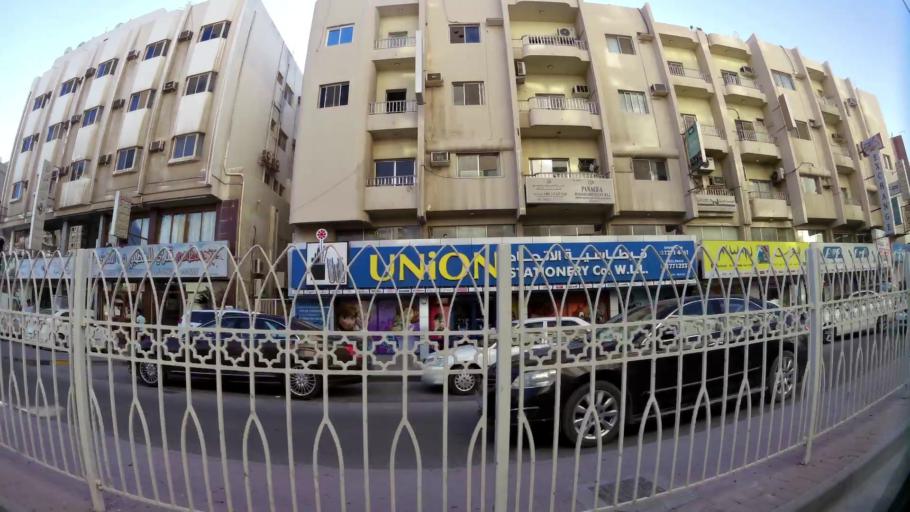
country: BH
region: Manama
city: Manama
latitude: 26.2270
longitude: 50.5964
